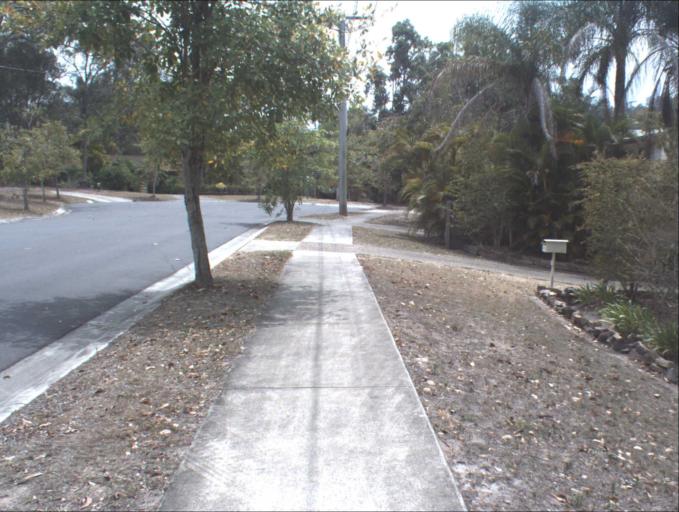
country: AU
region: Queensland
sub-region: Logan
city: Beenleigh
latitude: -27.6699
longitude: 153.1904
